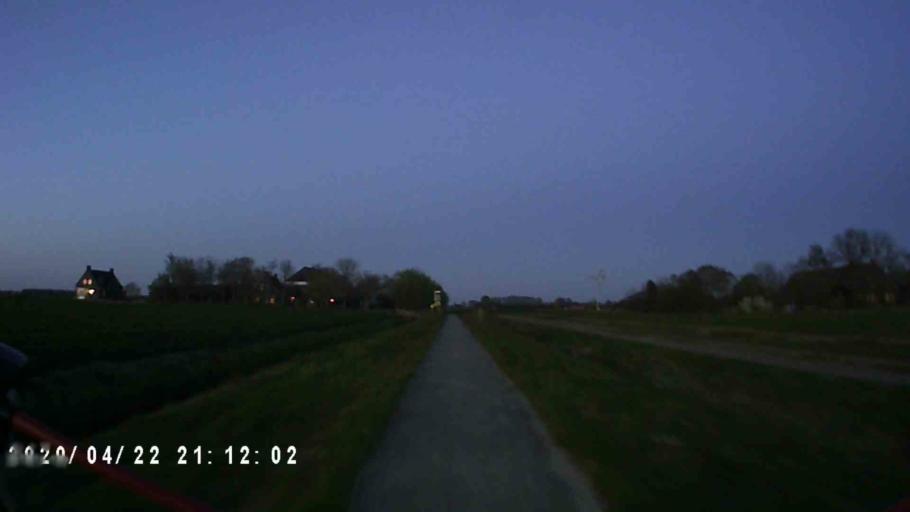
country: NL
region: Groningen
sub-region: Gemeente Bedum
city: Bedum
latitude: 53.3137
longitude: 6.5748
